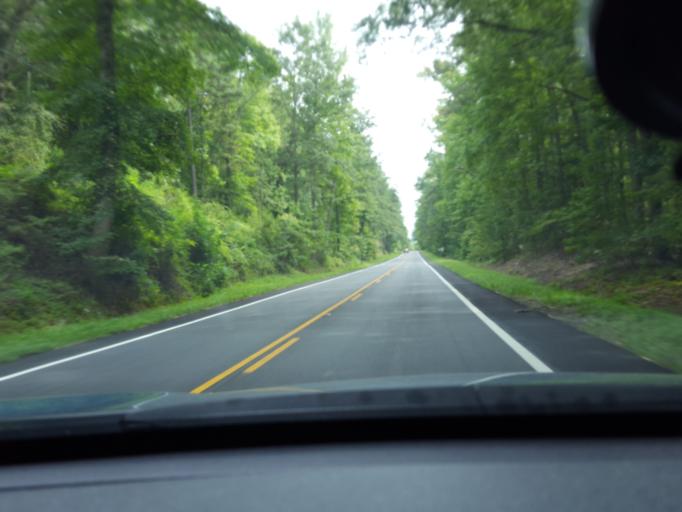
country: US
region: Virginia
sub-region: Hanover County
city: Hanover
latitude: 37.8088
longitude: -77.3736
